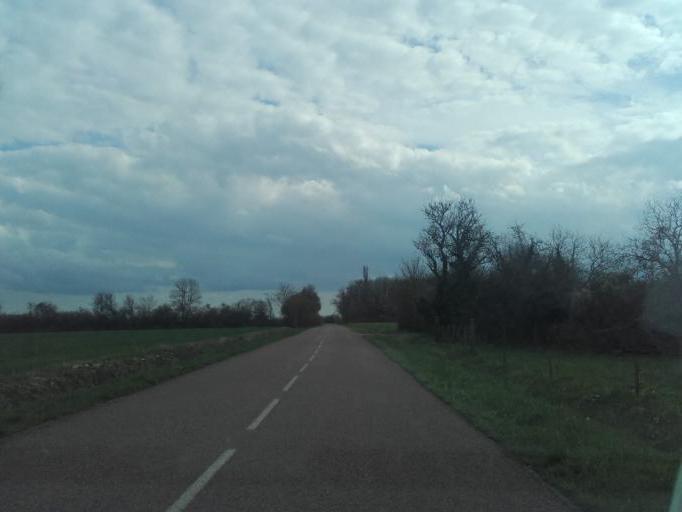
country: FR
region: Bourgogne
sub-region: Departement de la Cote-d'Or
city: Nolay
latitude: 46.9389
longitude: 4.6227
